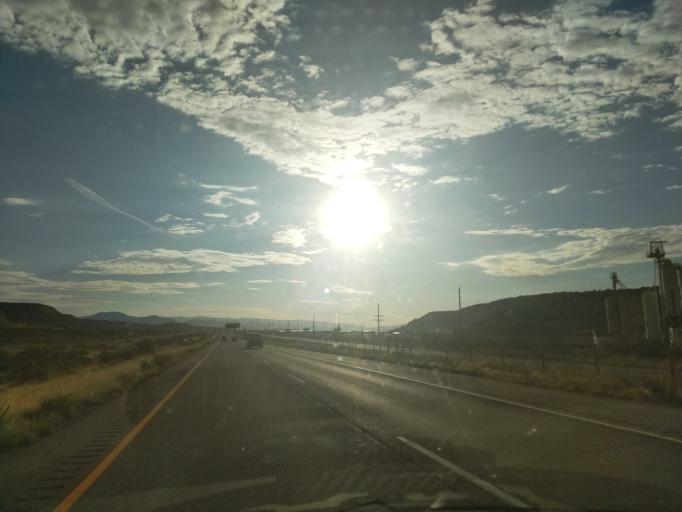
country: US
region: Colorado
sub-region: Garfield County
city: Rifle
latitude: 39.5154
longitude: -107.8611
